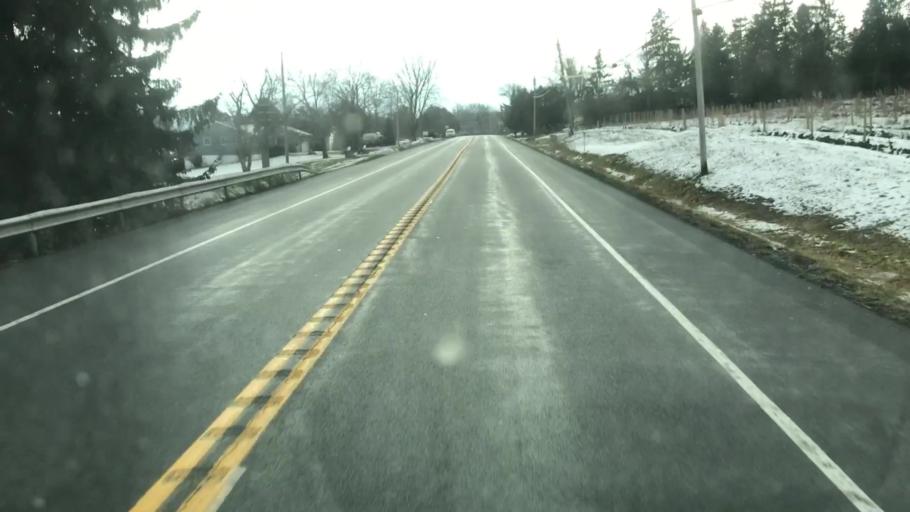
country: US
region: New York
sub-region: Onondaga County
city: Skaneateles
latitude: 42.8870
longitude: -76.4139
